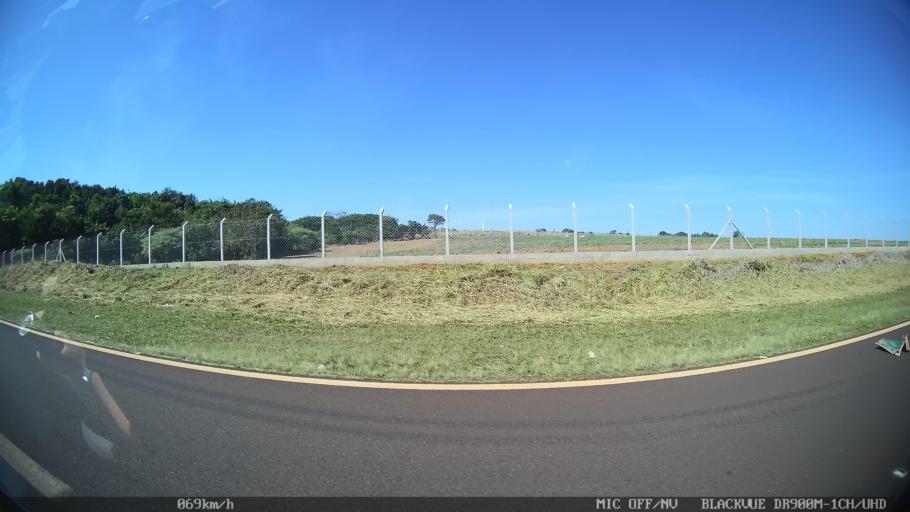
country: BR
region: Sao Paulo
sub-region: Batatais
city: Batatais
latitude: -20.8732
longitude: -47.6050
